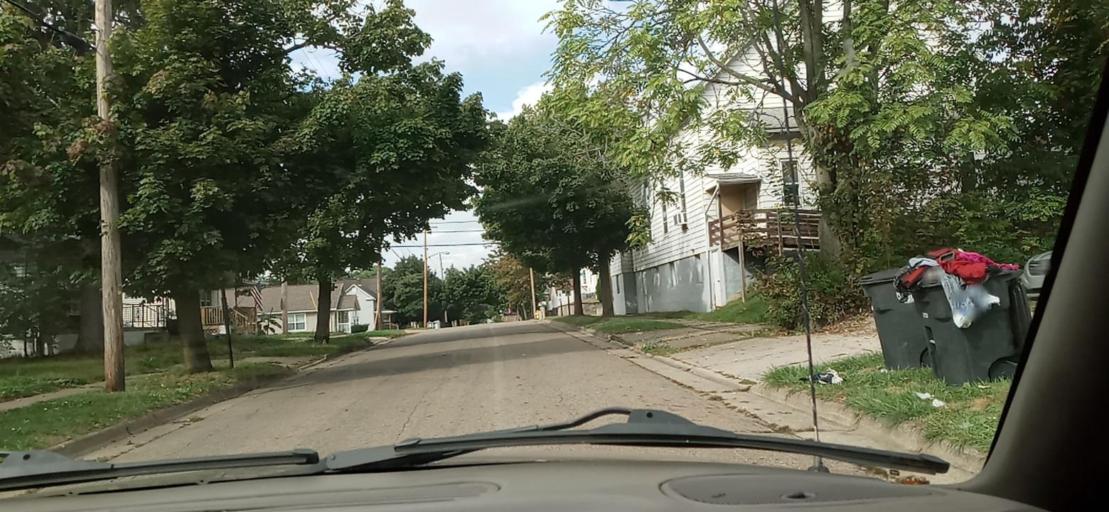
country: US
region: Ohio
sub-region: Summit County
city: Portage Lakes
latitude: 41.0420
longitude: -81.5525
